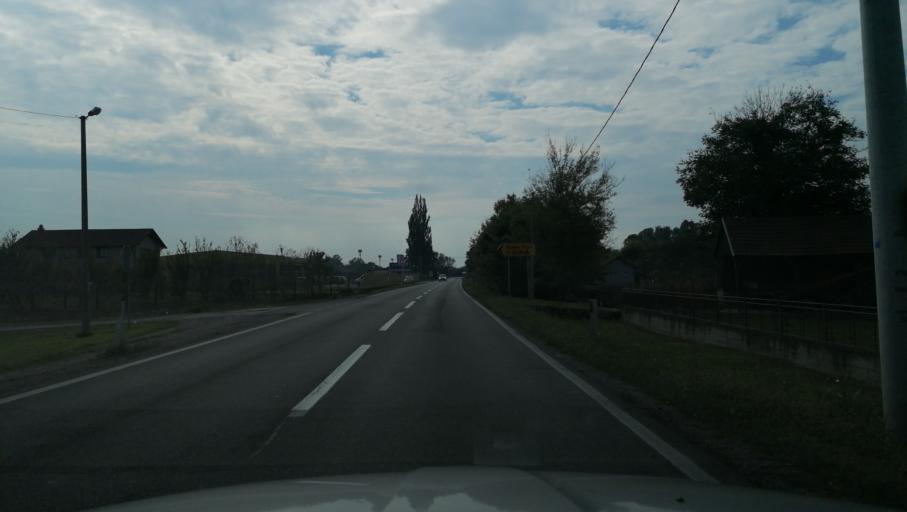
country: BA
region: Republika Srpska
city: Dvorovi
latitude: 44.8203
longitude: 19.2773
